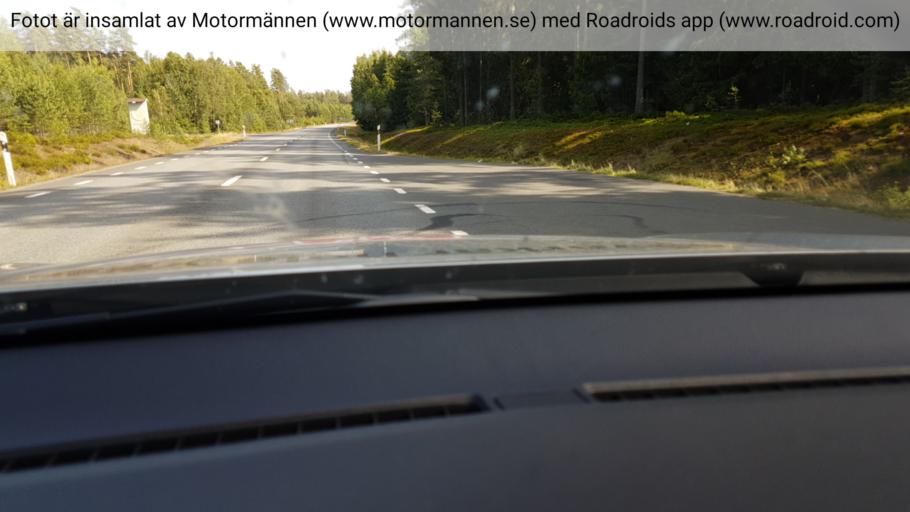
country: SE
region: Joenkoeping
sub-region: Eksjo Kommun
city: Eksjoe
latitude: 57.6466
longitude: 14.9560
